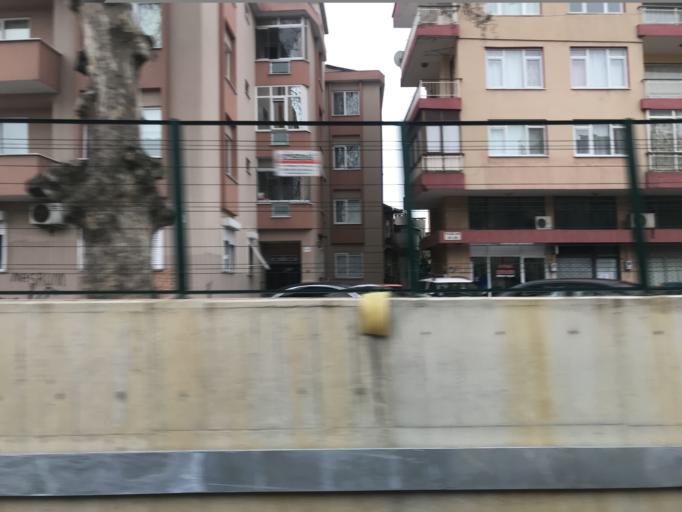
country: TR
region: Istanbul
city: Maltepe
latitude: 40.9219
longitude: 29.1304
